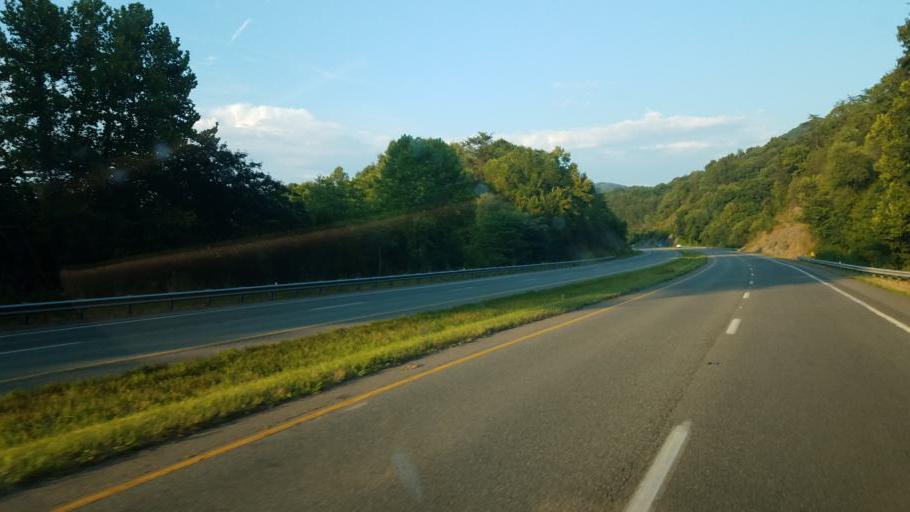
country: US
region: Virginia
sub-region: Scott County
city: Gate City
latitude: 36.6310
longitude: -82.5897
